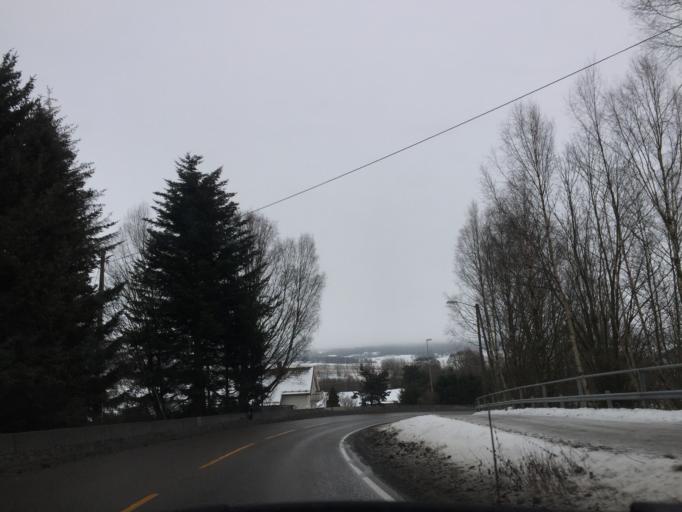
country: NO
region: Akershus
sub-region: Frogn
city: Drobak
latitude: 59.6864
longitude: 10.6666
